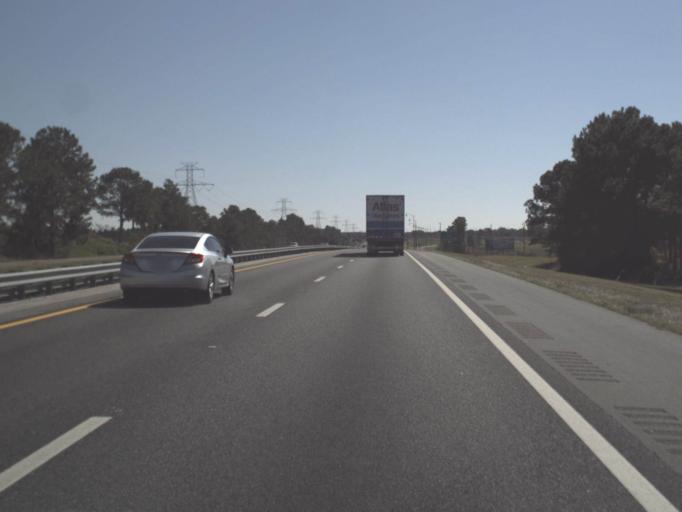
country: US
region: Florida
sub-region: Lake County
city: Hawthorne
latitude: 28.7638
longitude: -81.9478
